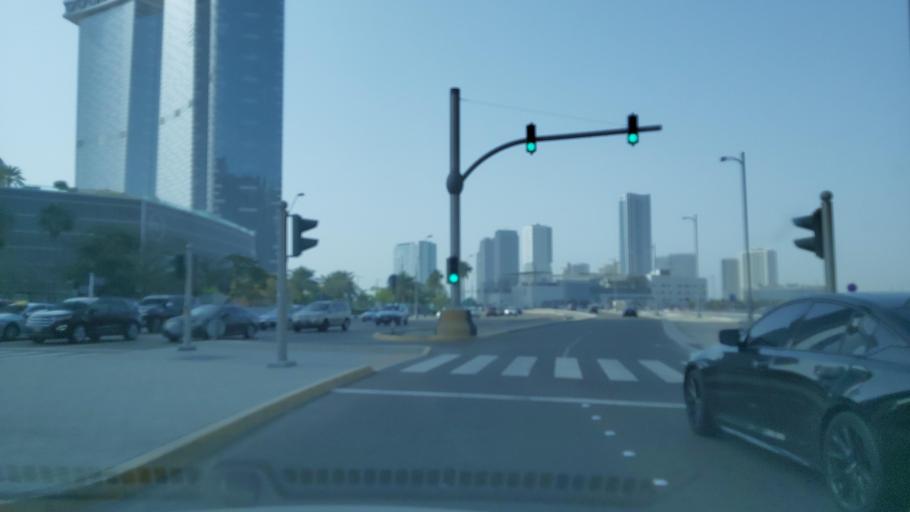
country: AE
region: Abu Dhabi
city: Abu Dhabi
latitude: 24.4968
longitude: 54.4056
